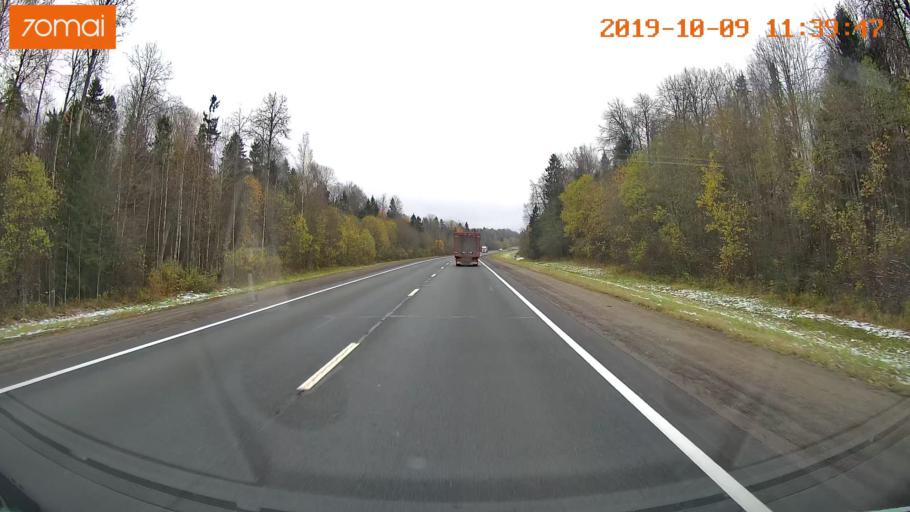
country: RU
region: Vologda
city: Gryazovets
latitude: 58.9519
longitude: 40.1694
